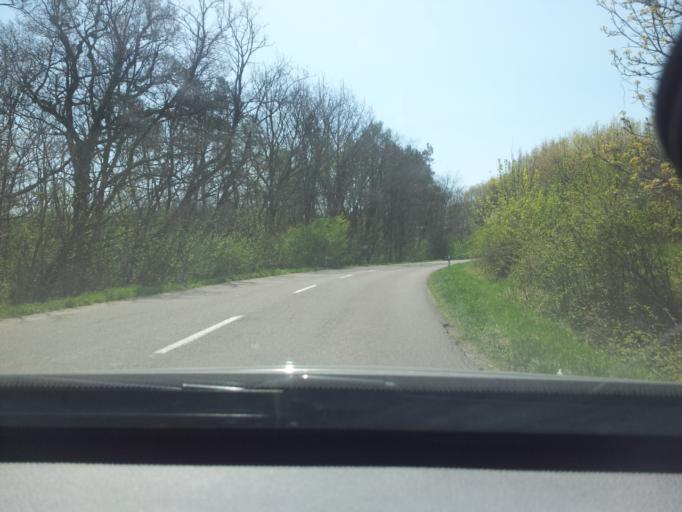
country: SK
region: Nitriansky
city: Tlmace
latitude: 48.3003
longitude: 18.4506
